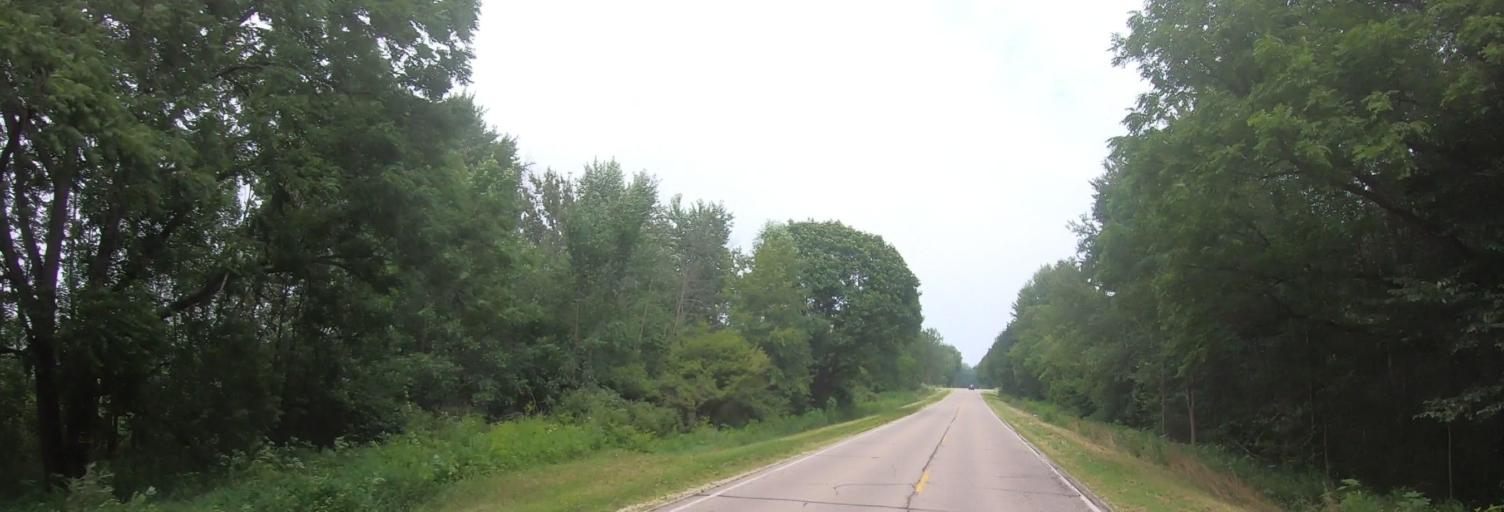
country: US
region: Michigan
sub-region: Shiawassee County
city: Corunna
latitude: 42.8670
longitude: -84.1115
